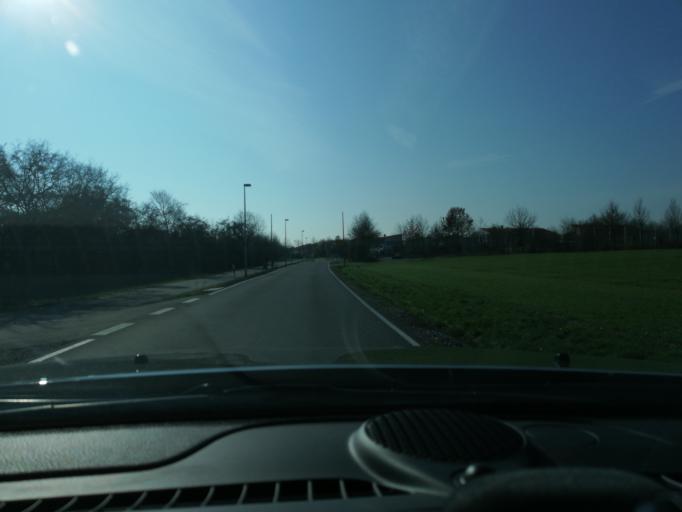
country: DE
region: Bavaria
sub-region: Regierungsbezirk Mittelfranken
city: Hessdorf
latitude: 49.5989
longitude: 10.9444
